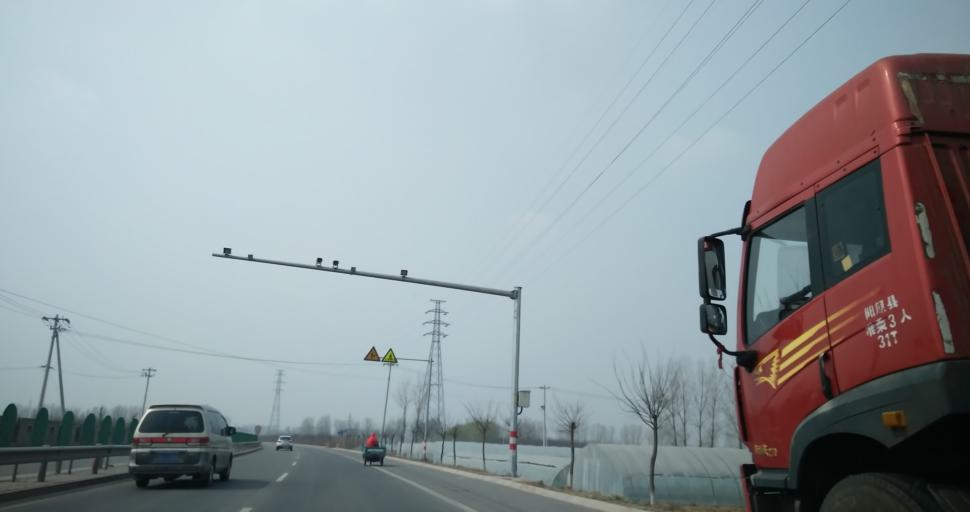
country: CN
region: Beijing
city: Qingyundian
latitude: 39.6916
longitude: 116.4711
